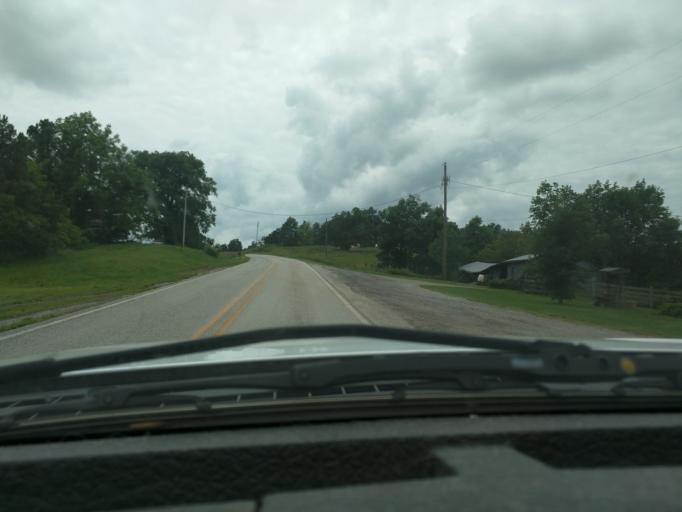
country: US
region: Arkansas
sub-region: Madison County
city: Huntsville
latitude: 35.8440
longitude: -93.5697
